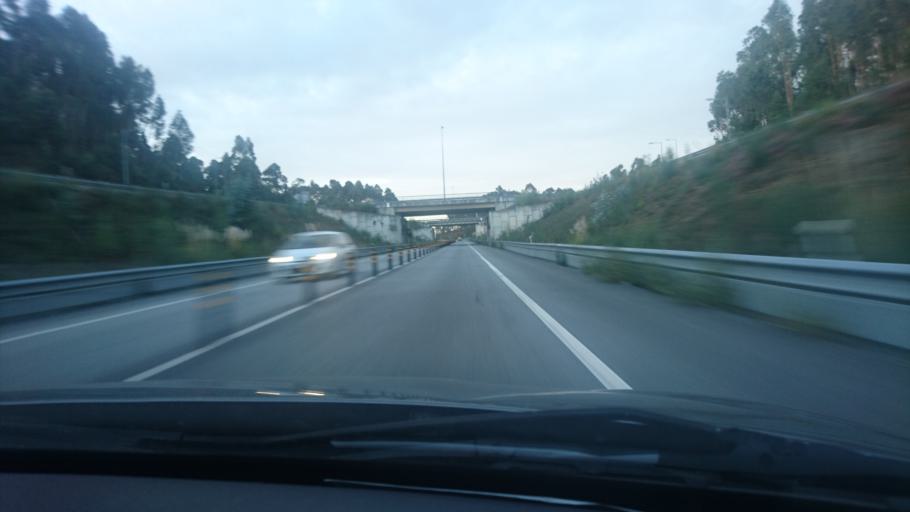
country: PT
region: Aveiro
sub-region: Santa Maria da Feira
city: Arrifana
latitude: 40.9255
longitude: -8.4869
